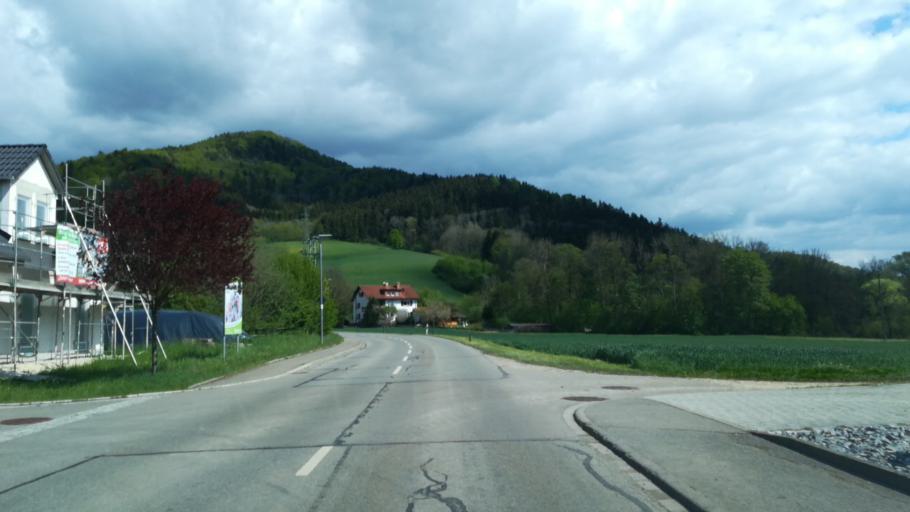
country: DE
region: Baden-Wuerttemberg
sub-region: Freiburg Region
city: Blumberg
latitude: 47.8354
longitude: 8.5041
